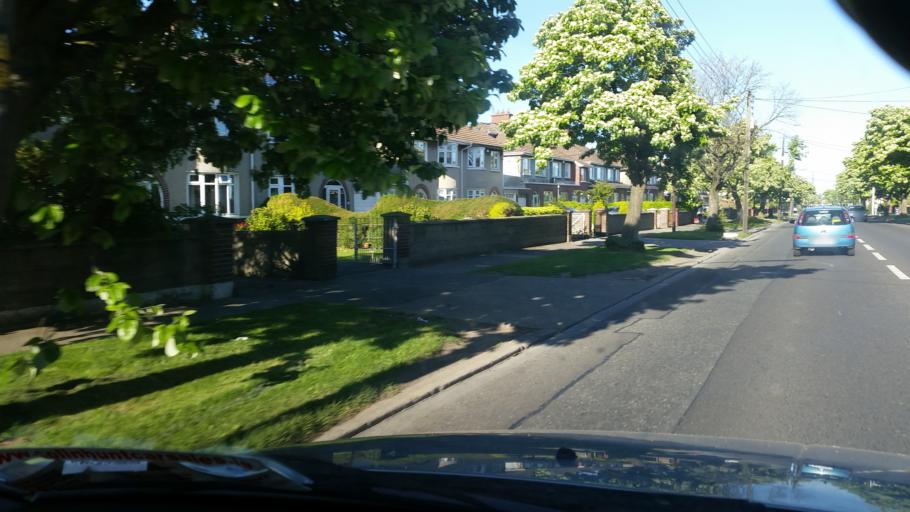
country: IE
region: Leinster
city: Ballymun
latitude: 53.3903
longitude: -6.2762
